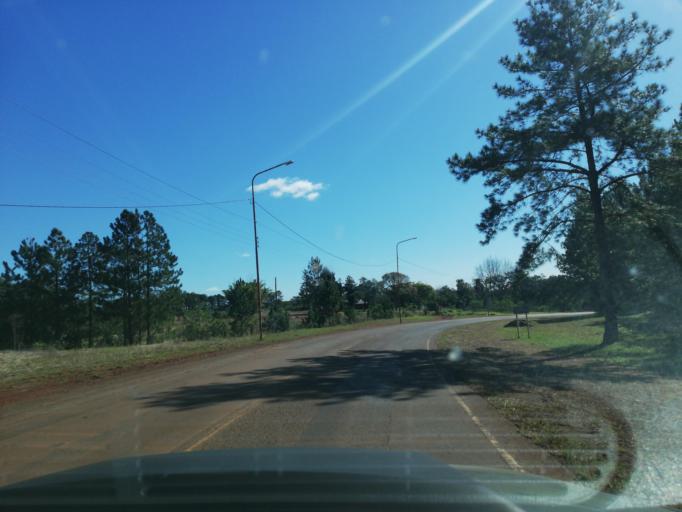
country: AR
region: Misiones
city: Aristobulo del Valle
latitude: -27.0895
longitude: -54.9151
